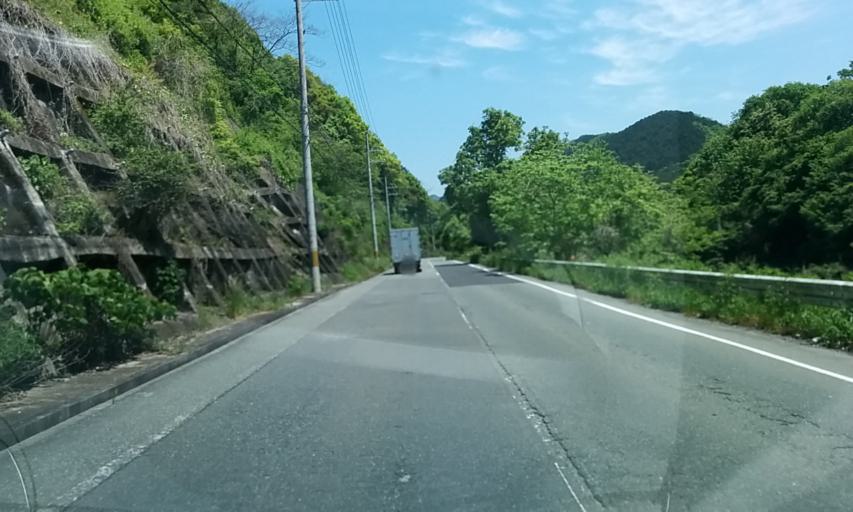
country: JP
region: Kyoto
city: Ayabe
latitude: 35.2250
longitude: 135.2317
